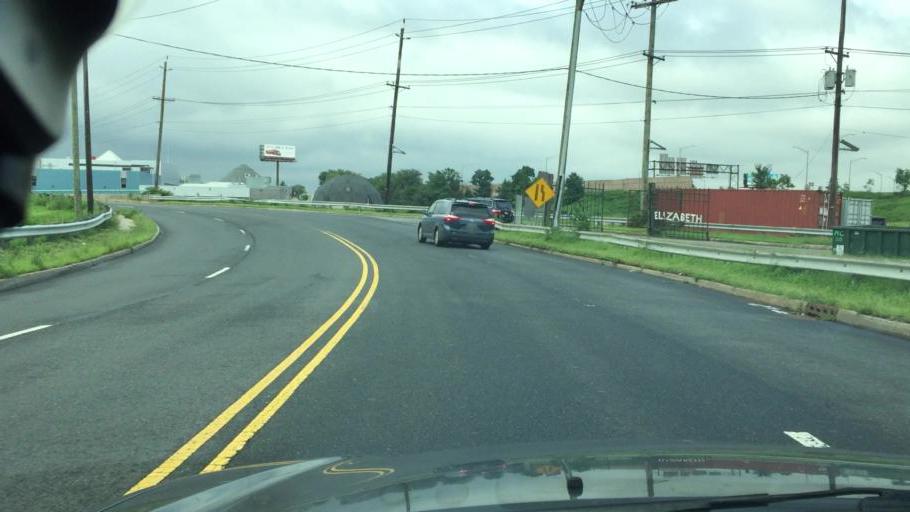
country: US
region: New Jersey
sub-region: Union County
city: Elizabeth
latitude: 40.6468
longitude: -74.2059
